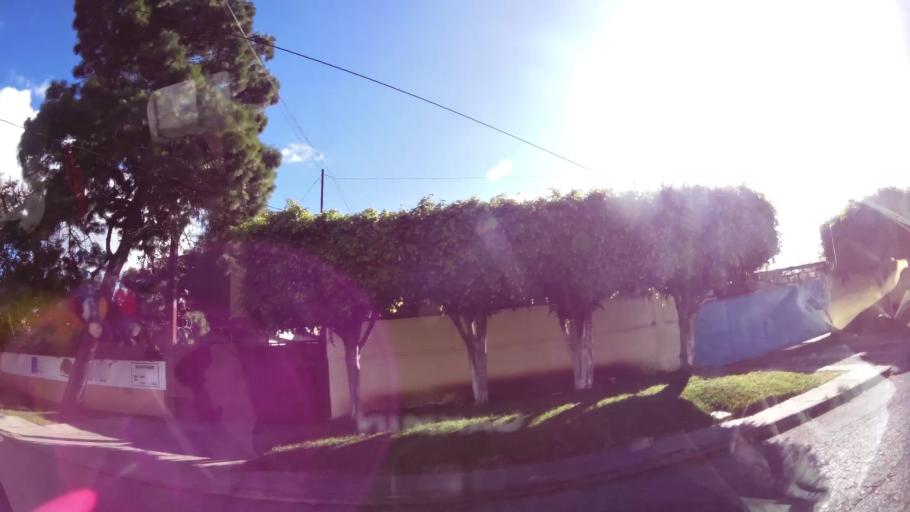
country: GT
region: Guatemala
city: Guatemala City
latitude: 14.6070
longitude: -90.5540
